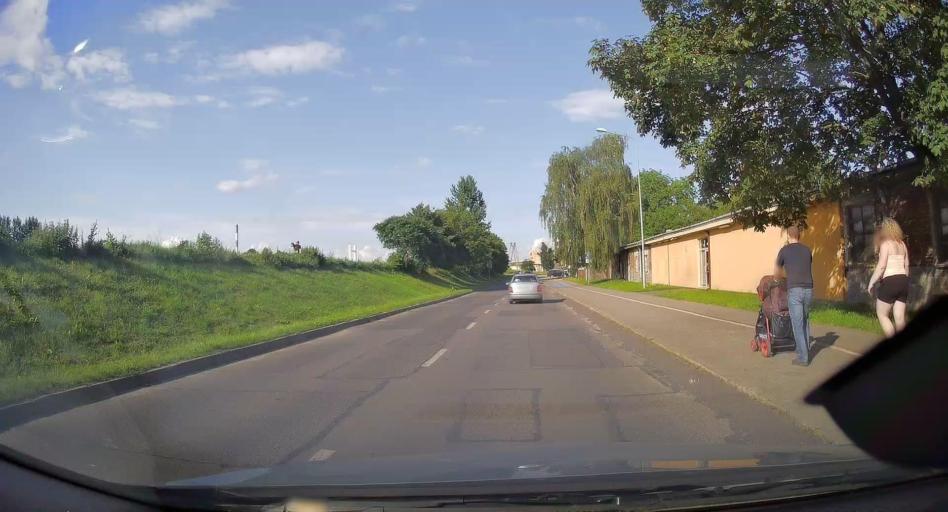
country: PL
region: Subcarpathian Voivodeship
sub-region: Przemysl
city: Przemysl
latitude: 49.7891
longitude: 22.7782
